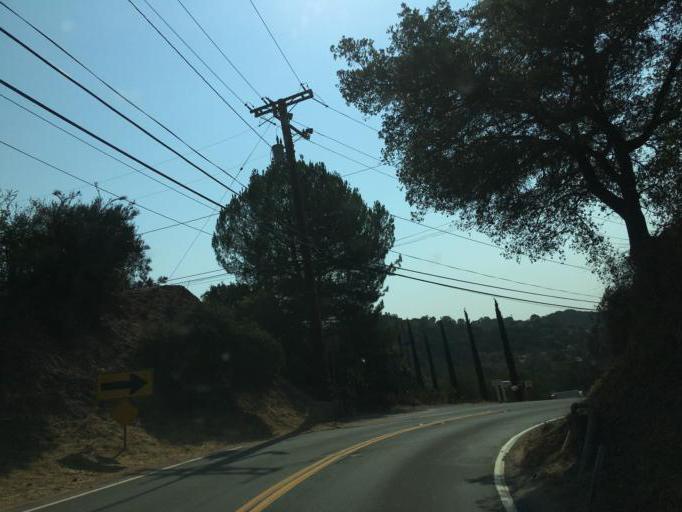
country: US
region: California
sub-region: Los Angeles County
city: Topanga
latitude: 34.1116
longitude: -118.6323
